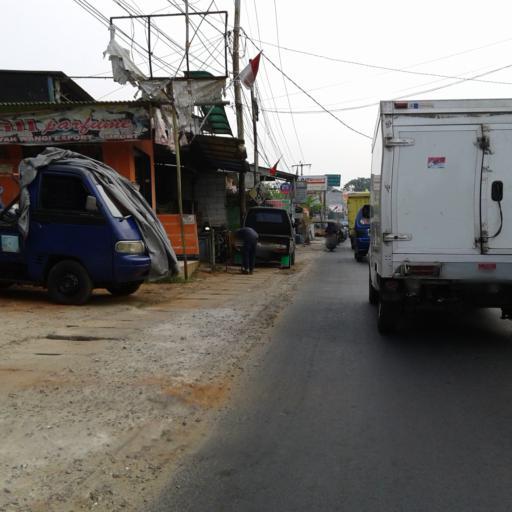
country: ID
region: West Java
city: Sawangan
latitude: -6.4017
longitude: 106.7714
